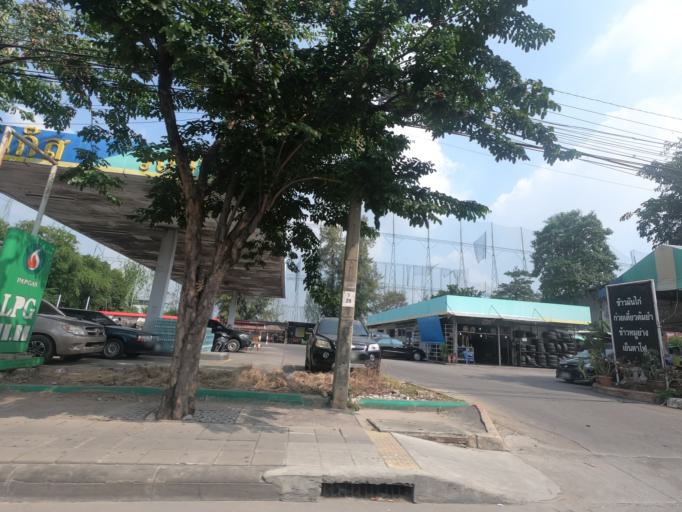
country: TH
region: Bangkok
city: Lat Phrao
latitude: 13.8242
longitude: 100.6099
